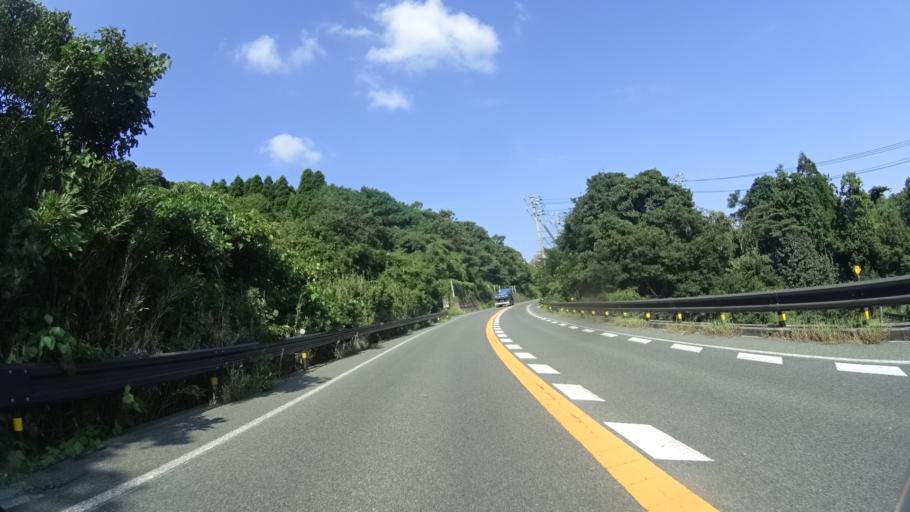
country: JP
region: Shimane
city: Gotsucho
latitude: 35.0358
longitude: 132.2635
